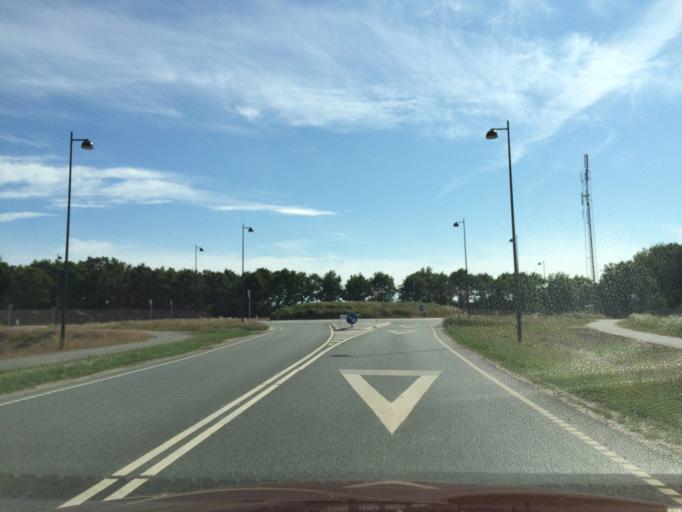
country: DK
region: Central Jutland
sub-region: Silkeborg Kommune
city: Silkeborg
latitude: 56.1982
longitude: 9.5469
